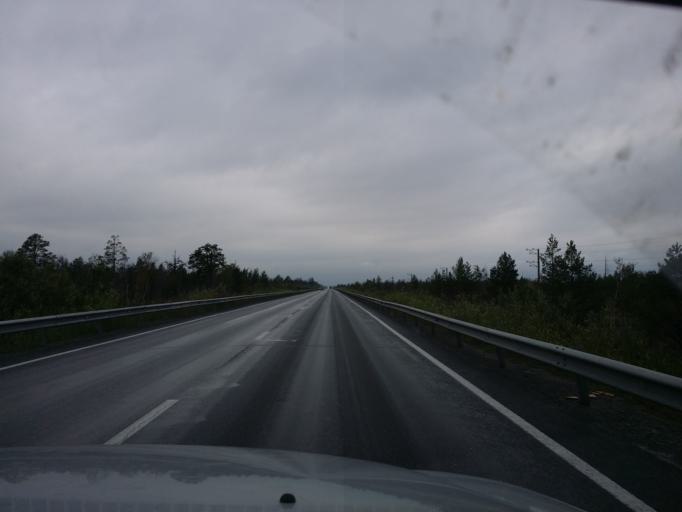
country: RU
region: Khanty-Mansiyskiy Avtonomnyy Okrug
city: Lokosovo
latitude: 61.4512
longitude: 74.7114
